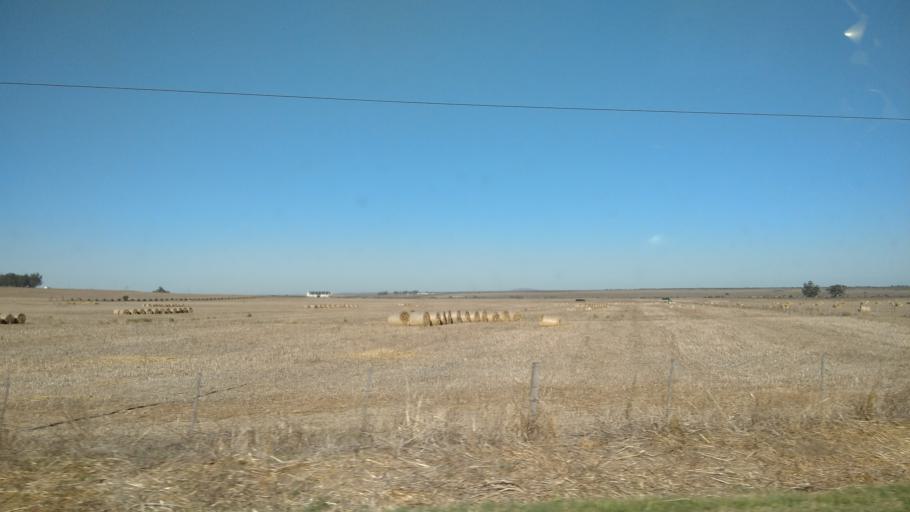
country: ZA
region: Western Cape
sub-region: West Coast District Municipality
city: Moorreesburg
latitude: -33.1258
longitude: 18.4456
